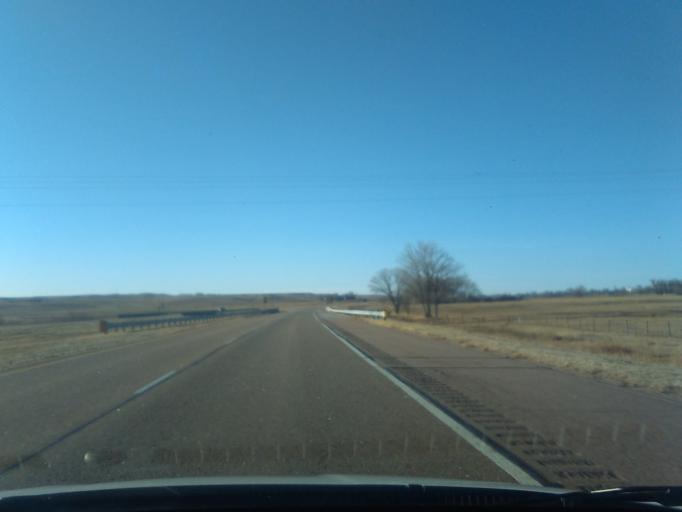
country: US
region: Nebraska
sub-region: Deuel County
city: Chappell
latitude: 41.0574
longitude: -102.4284
